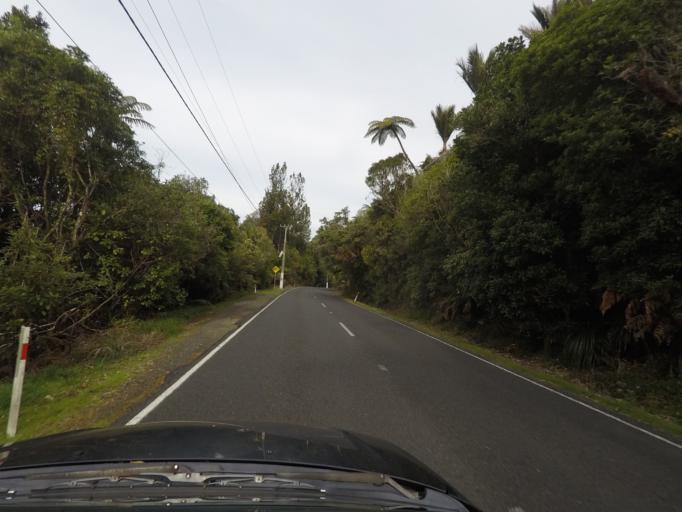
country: NZ
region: Auckland
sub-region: Auckland
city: Titirangi
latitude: -36.9354
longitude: 174.5789
